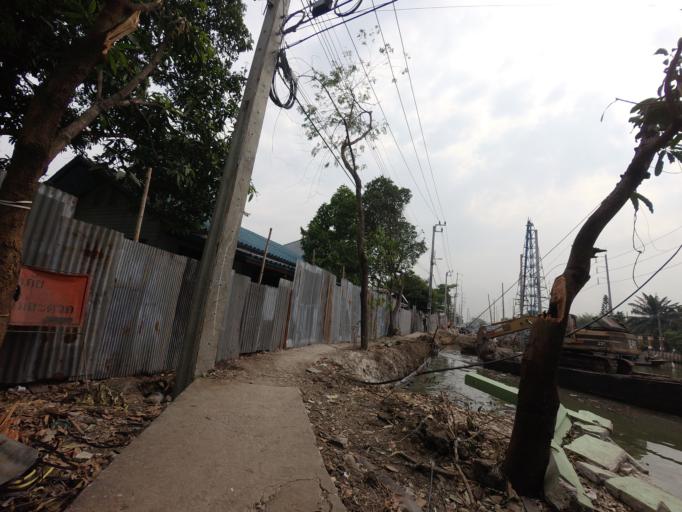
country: TH
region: Bangkok
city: Suan Luang
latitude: 13.7241
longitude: 100.6897
